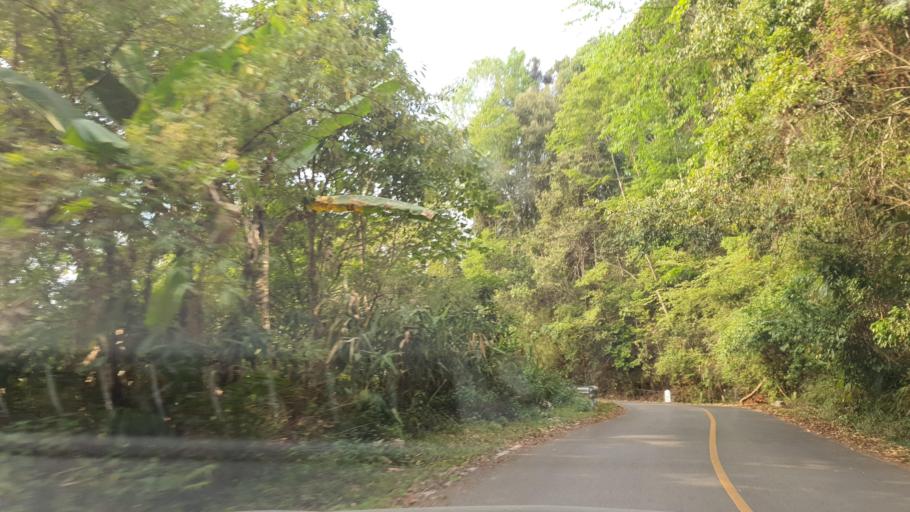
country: TH
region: Lampang
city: Mueang Pan
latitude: 18.9355
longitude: 99.3824
